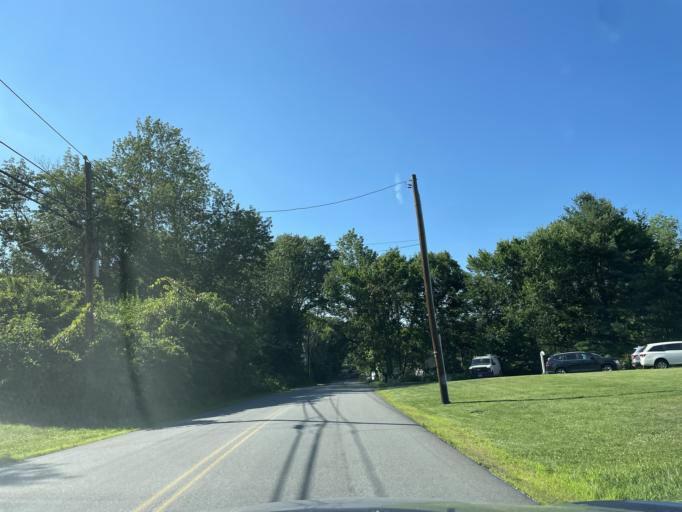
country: US
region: Massachusetts
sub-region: Worcester County
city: Charlton
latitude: 42.1627
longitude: -72.0233
